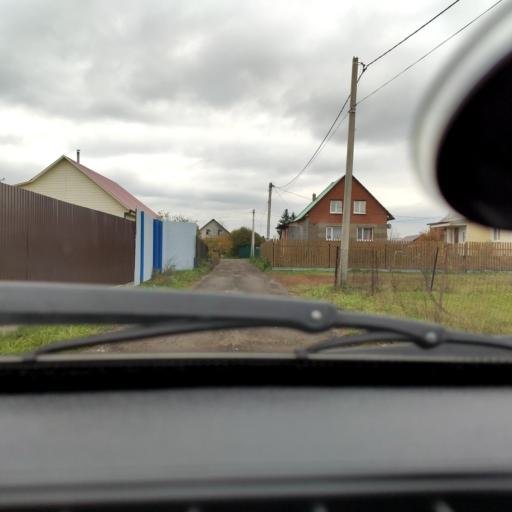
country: RU
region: Bashkortostan
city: Mikhaylovka
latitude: 54.7643
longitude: 55.9047
